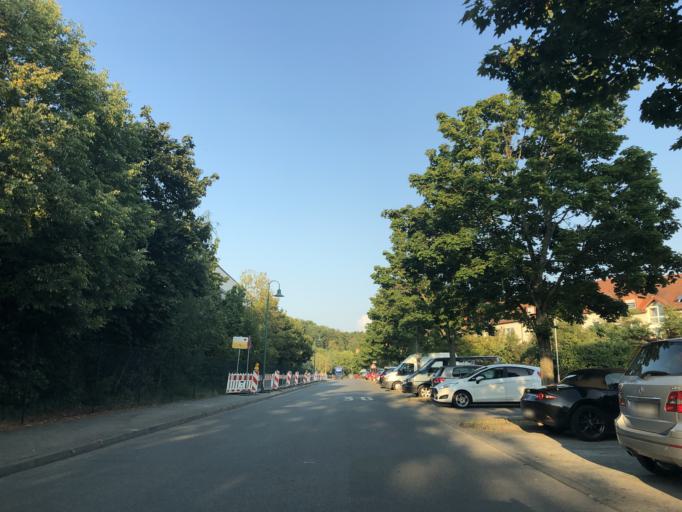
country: DE
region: Hesse
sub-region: Regierungsbezirk Darmstadt
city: Darmstadt
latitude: 49.9028
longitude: 8.6827
